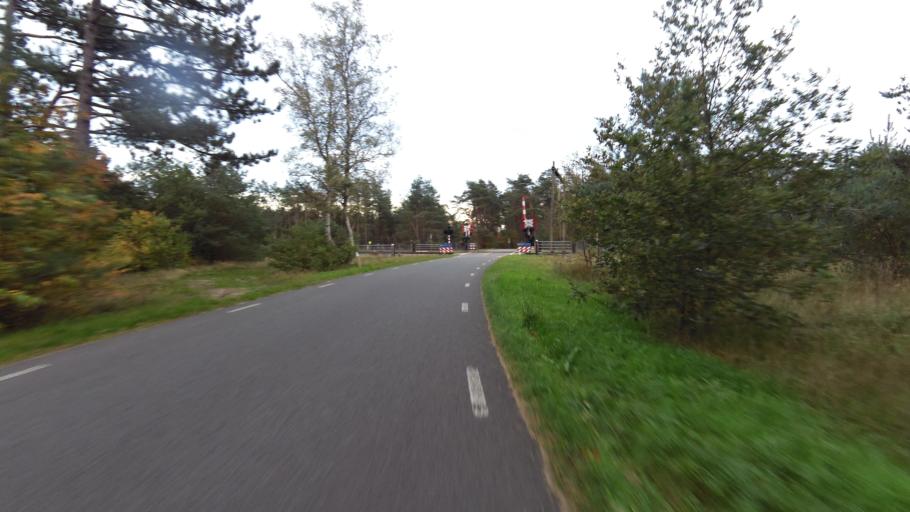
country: NL
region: Gelderland
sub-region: Gemeente Nunspeet
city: Nunspeet
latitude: 52.3824
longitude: 5.8340
